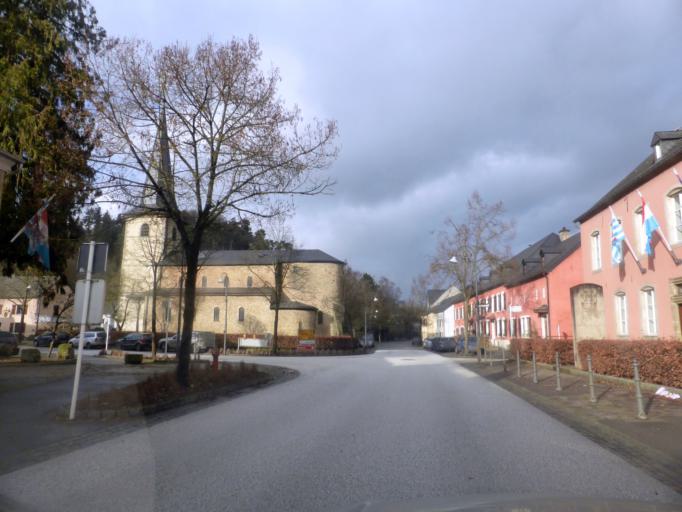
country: LU
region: Diekirch
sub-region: Canton de Redange
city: Saeul
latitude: 49.7245
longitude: 5.9852
